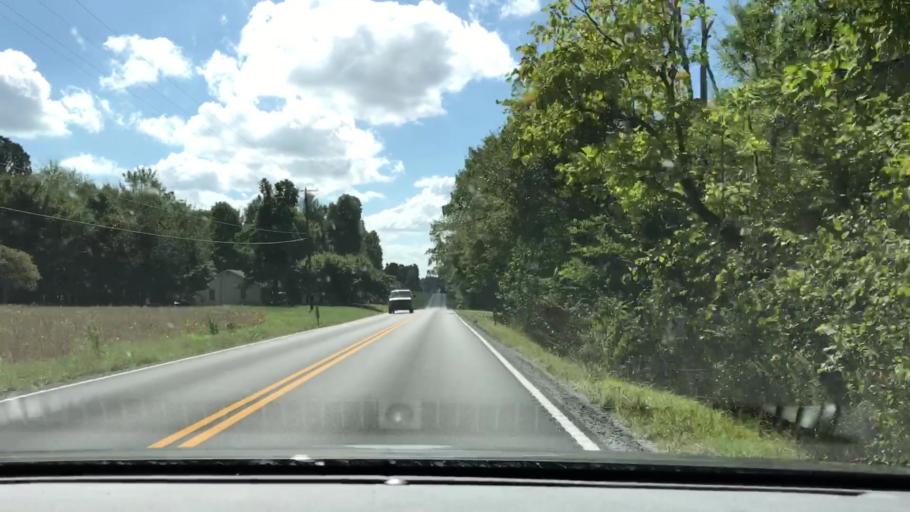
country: US
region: Kentucky
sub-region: Graves County
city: Mayfield
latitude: 36.7946
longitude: -88.5955
